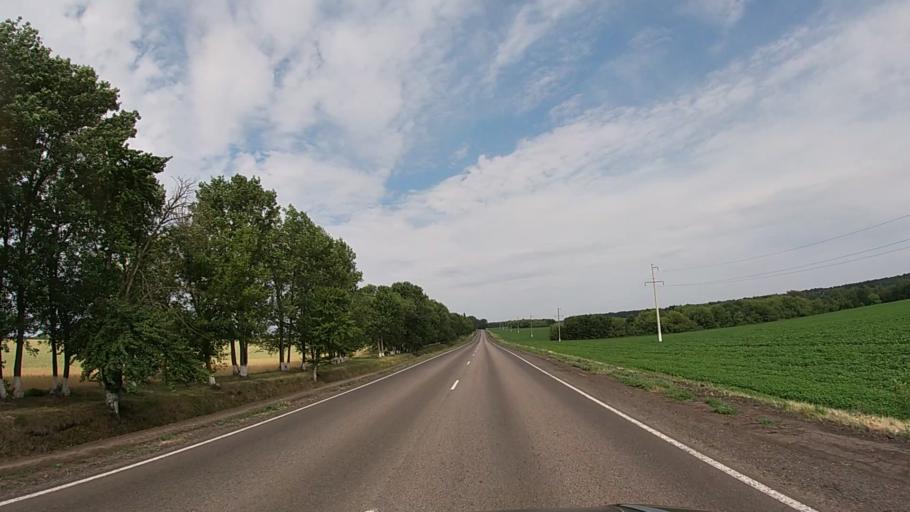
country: RU
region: Belgorod
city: Krasnaya Yaruga
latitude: 50.8094
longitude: 35.5213
